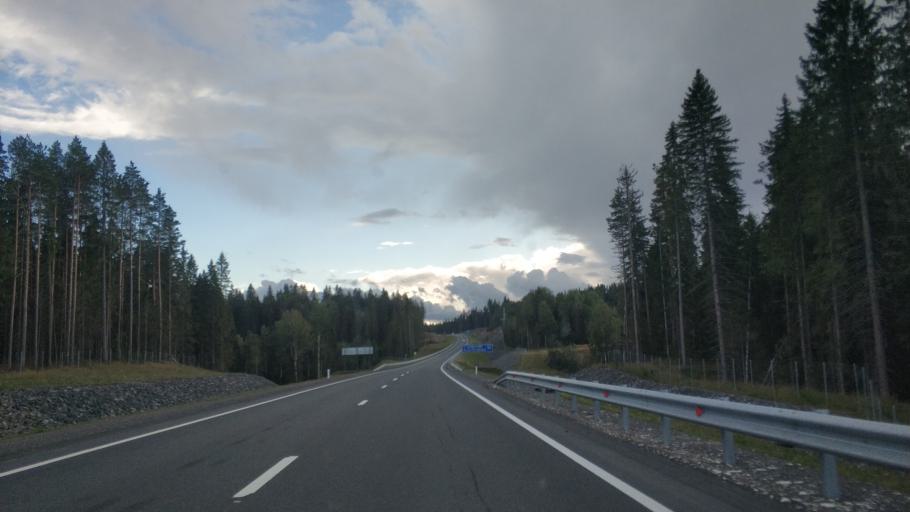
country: RU
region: Republic of Karelia
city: Lakhdenpokh'ya
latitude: 61.4728
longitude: 30.0059
